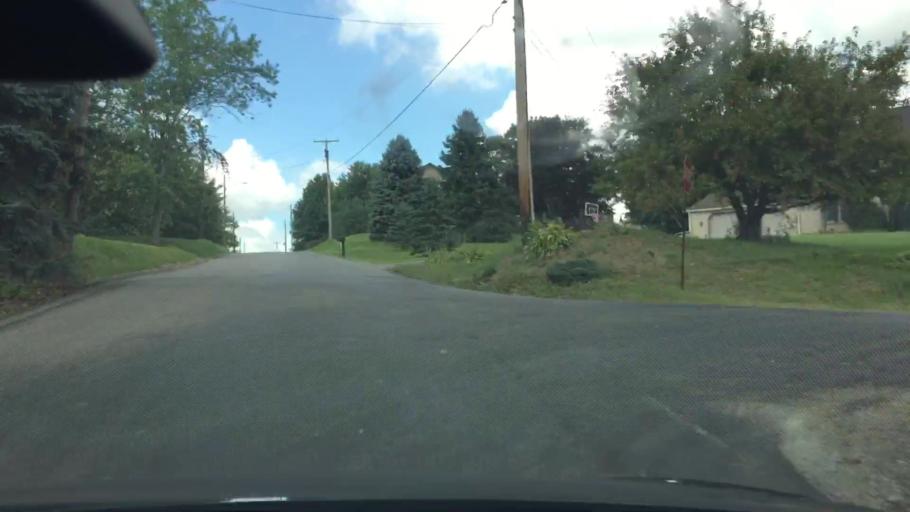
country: US
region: Pennsylvania
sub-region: Butler County
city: Meadowood
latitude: 40.8178
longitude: -79.8748
